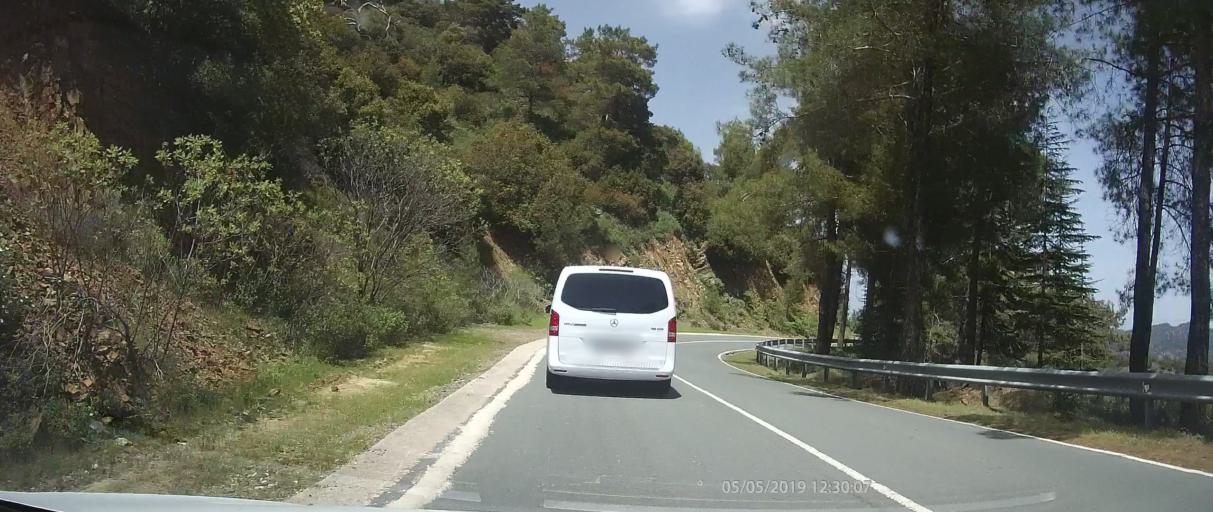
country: CY
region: Lefkosia
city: Kakopetria
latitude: 34.9821
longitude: 32.7487
